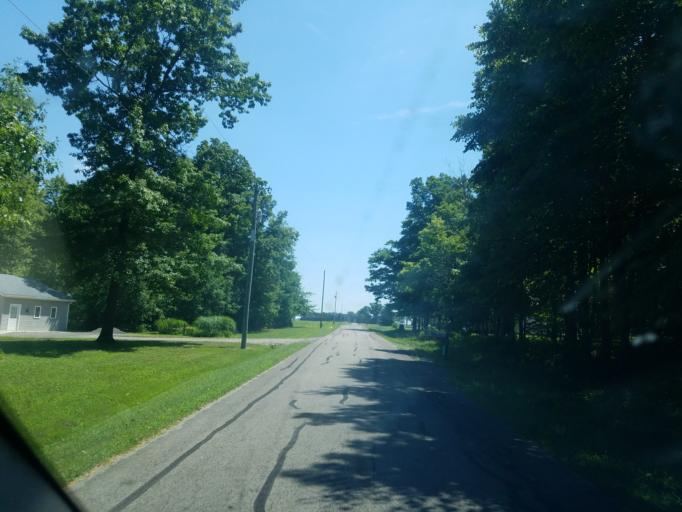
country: US
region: Ohio
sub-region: Hancock County
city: Arlington
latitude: 40.8630
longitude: -83.7190
